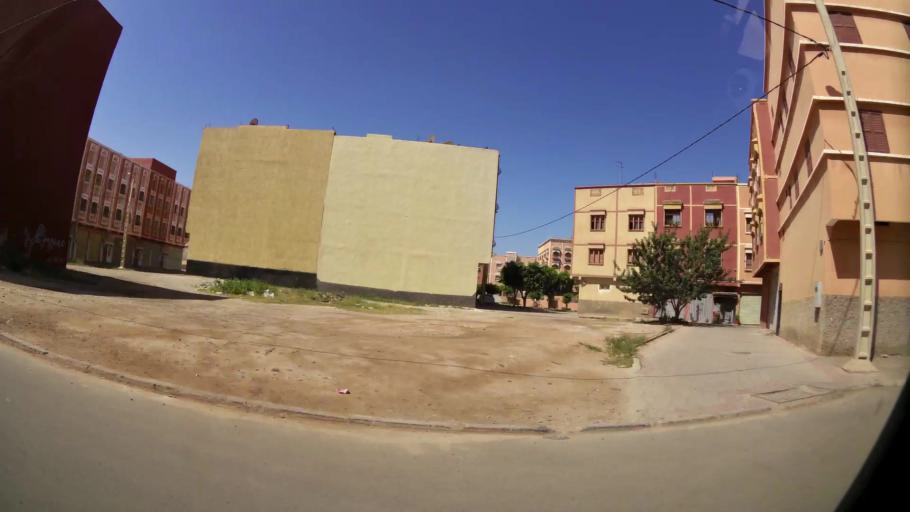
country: MA
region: Souss-Massa-Draa
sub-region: Inezgane-Ait Mellou
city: Inezgane
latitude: 30.3334
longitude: -9.5068
